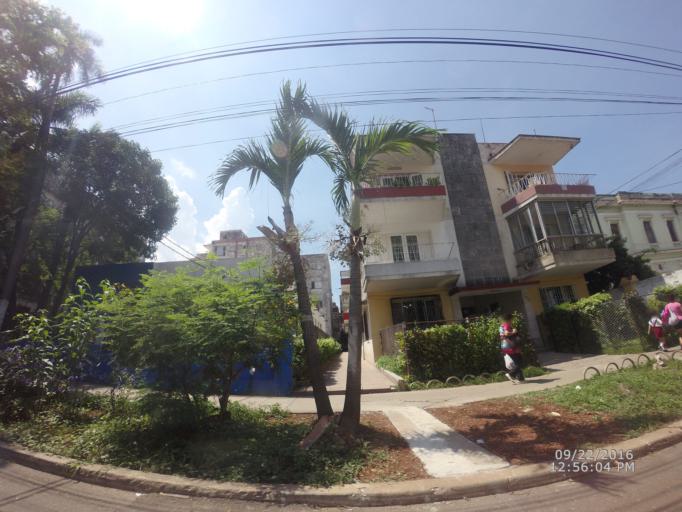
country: CU
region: La Habana
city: Havana
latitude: 23.1420
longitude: -82.3885
